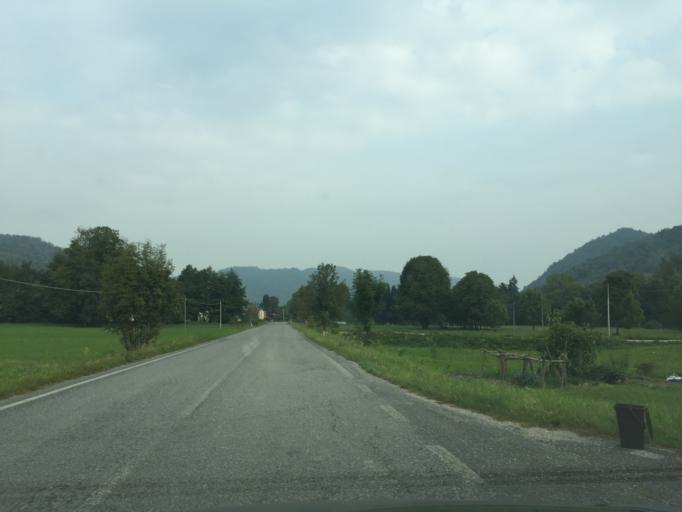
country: IT
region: Piedmont
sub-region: Provincia di Cuneo
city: Roccaforte Mondovi
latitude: 44.2968
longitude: 7.7467
